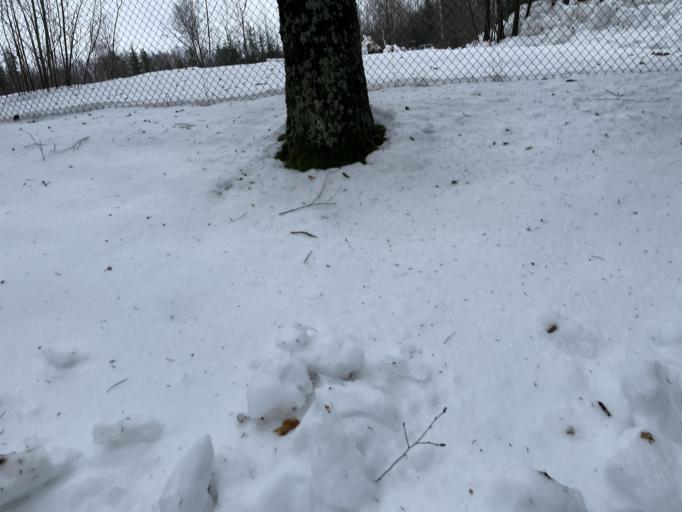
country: LV
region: Ludzas Rajons
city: Ludza
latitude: 56.4476
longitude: 27.6353
